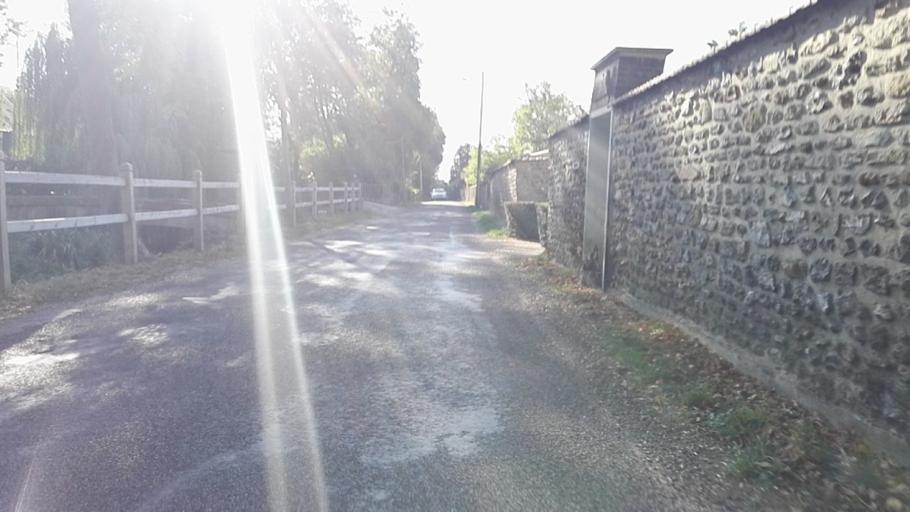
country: FR
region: Haute-Normandie
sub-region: Departement de l'Eure
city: Houlbec-Cocherel
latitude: 49.0550
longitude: 1.3349
